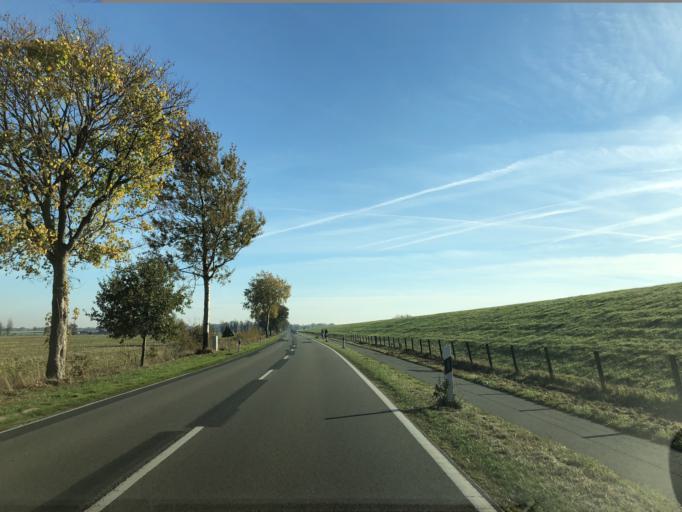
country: DE
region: Lower Saxony
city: Rhede
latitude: 53.0598
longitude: 7.2964
